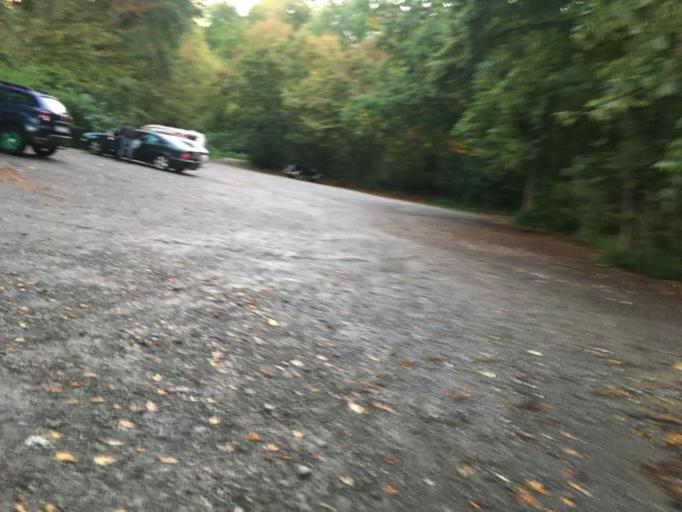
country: DE
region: North Rhine-Westphalia
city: Hattingen
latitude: 51.4332
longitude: 7.1260
